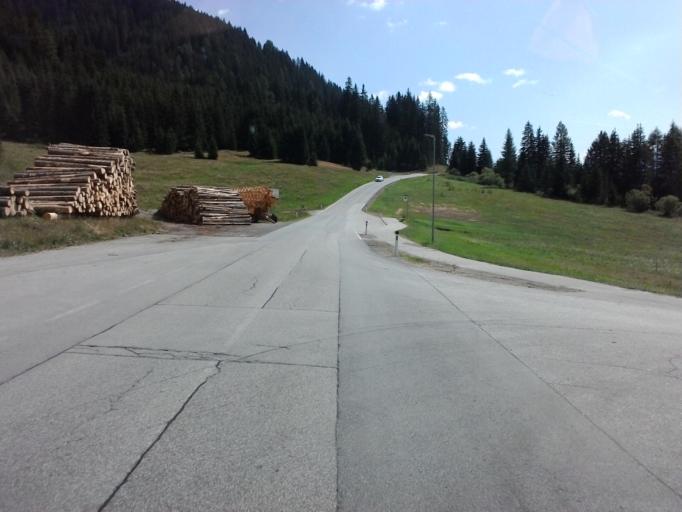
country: AT
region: Tyrol
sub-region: Politischer Bezirk Lienz
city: Obertilliach
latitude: 46.7104
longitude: 12.5926
